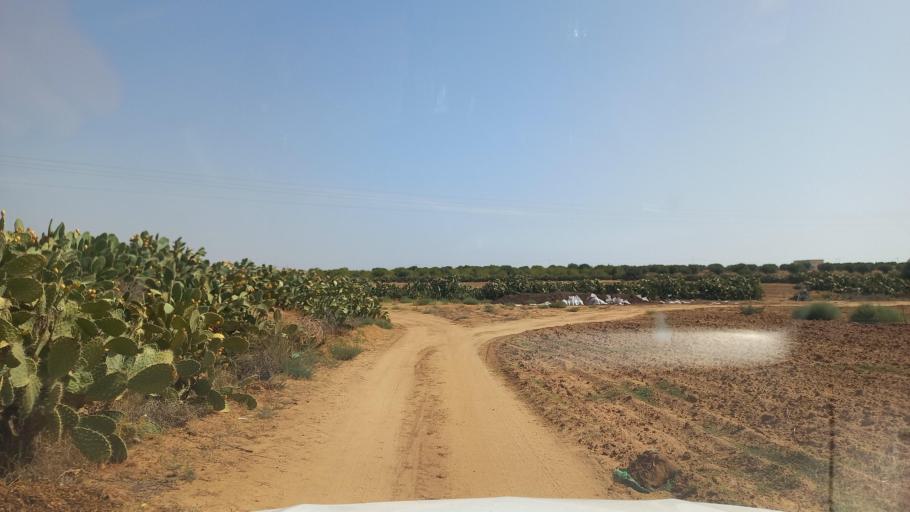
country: TN
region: Al Qasrayn
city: Kasserine
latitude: 35.2437
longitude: 9.0595
